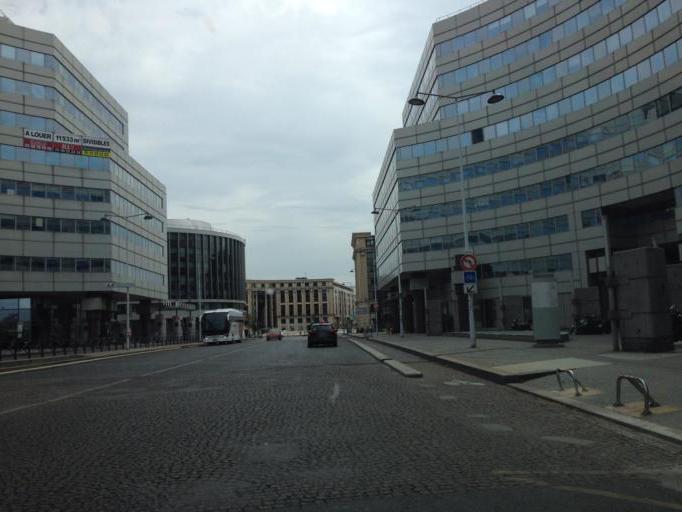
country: FR
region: Ile-de-France
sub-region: Departement des Hauts-de-Seine
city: Montrouge
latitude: 48.8387
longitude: 2.3168
